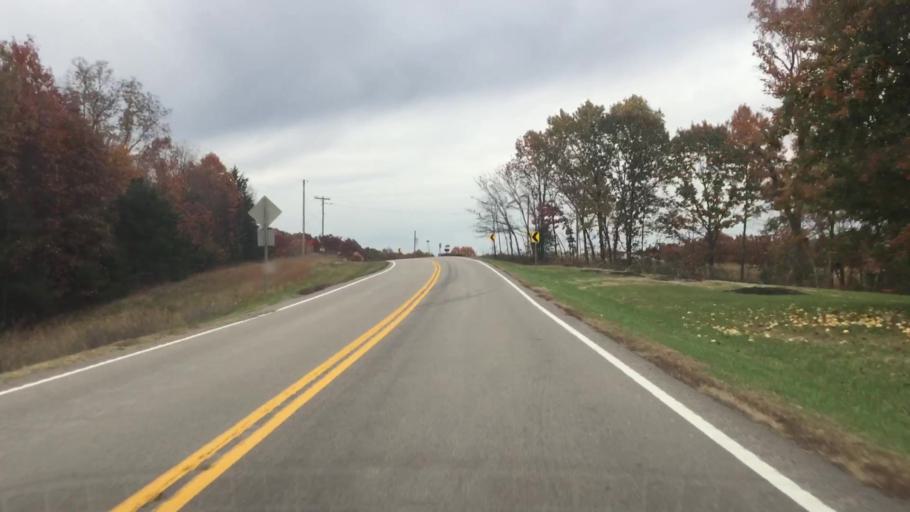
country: US
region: Missouri
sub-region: Gasconade County
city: Hermann
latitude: 38.7171
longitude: -91.6417
